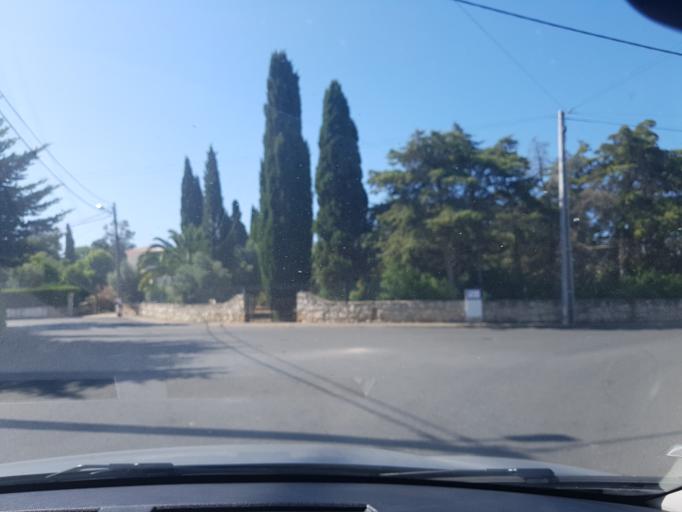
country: PT
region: Faro
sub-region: Lagoa
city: Carvoeiro
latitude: 37.0989
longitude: -8.4628
